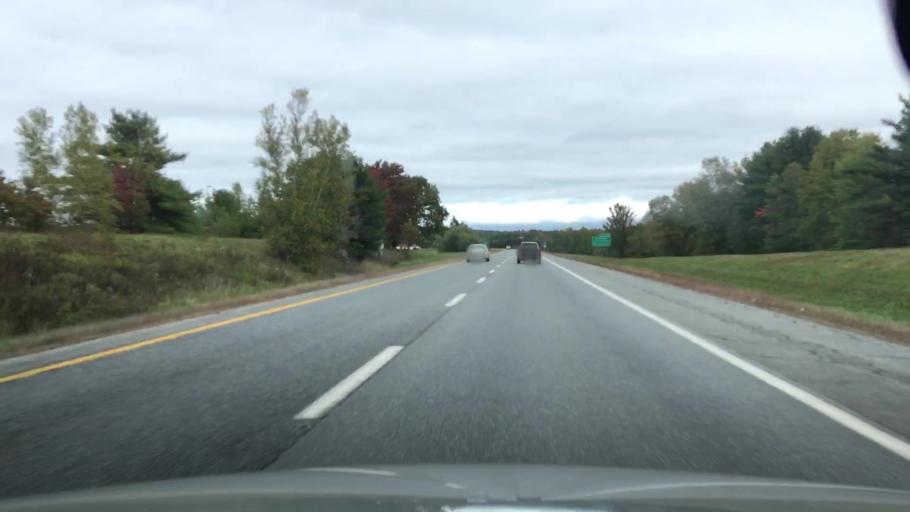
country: US
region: Maine
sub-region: Penobscot County
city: Brewer
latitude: 44.8254
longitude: -68.7539
